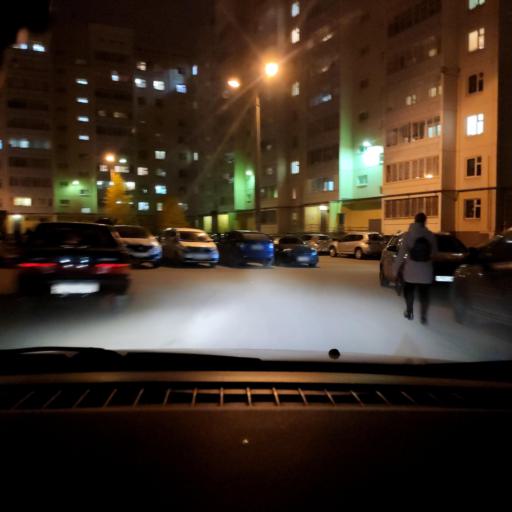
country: RU
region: Perm
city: Kondratovo
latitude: 58.0349
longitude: 56.1375
